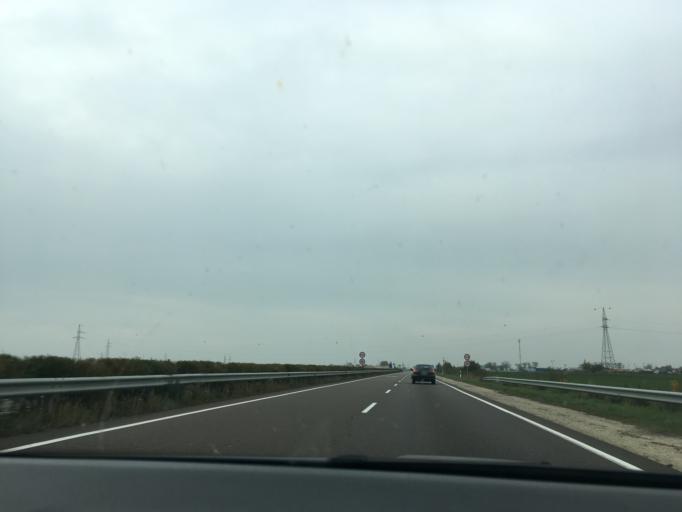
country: HU
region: Pest
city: Cegled
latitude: 47.1949
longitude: 19.8228
